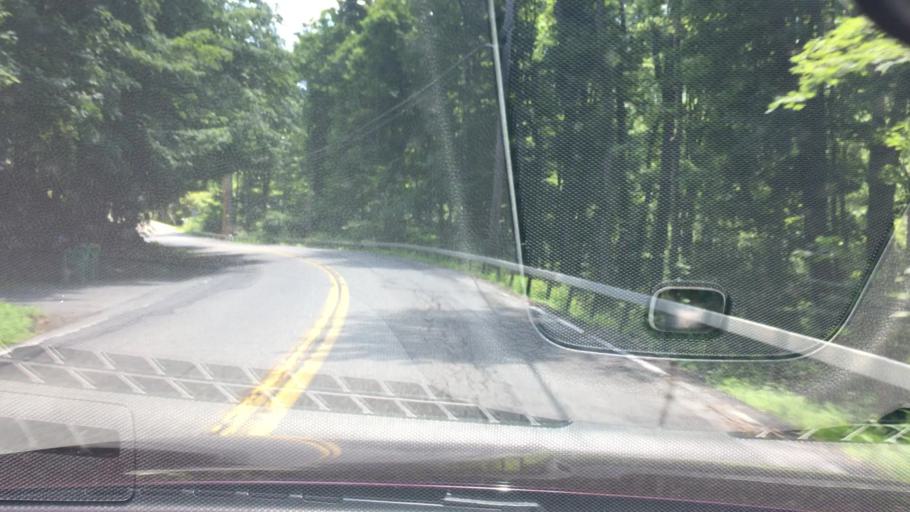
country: US
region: New York
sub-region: Putnam County
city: Lake Carmel
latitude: 41.4880
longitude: -73.6570
